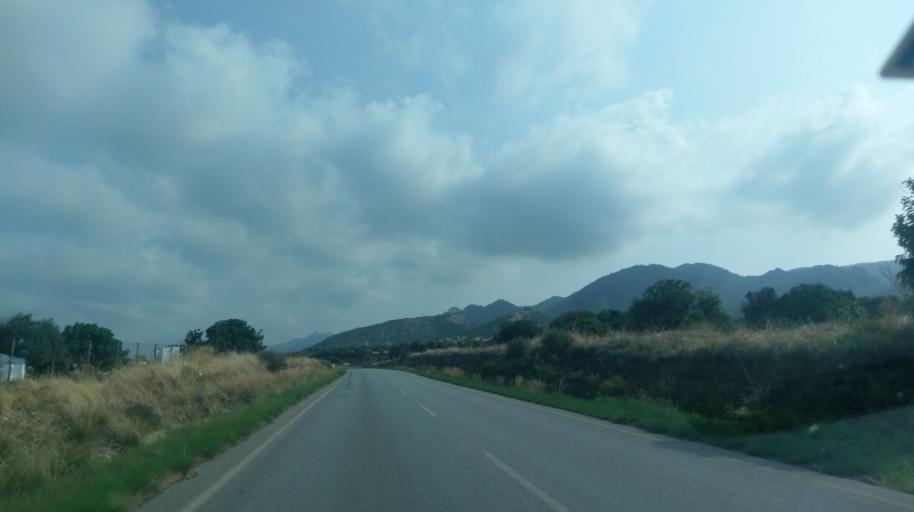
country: CY
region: Ammochostos
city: Lefkonoiko
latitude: 35.3535
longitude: 33.6404
